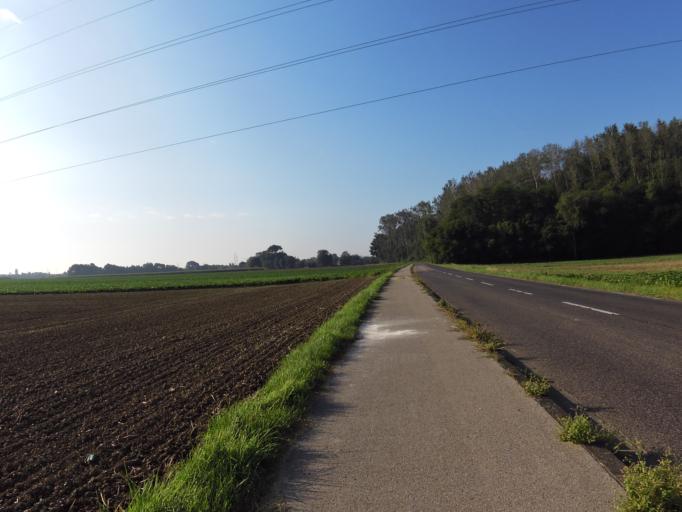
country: DE
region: North Rhine-Westphalia
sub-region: Regierungsbezirk Koln
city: Ubach-Palenberg
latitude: 50.9283
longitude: 6.1232
